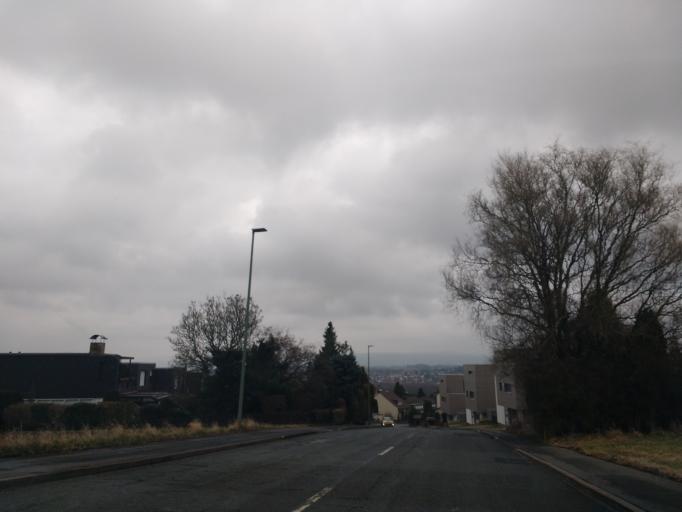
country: DE
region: Hesse
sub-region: Regierungsbezirk Kassel
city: Baunatal
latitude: 51.2827
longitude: 9.4233
